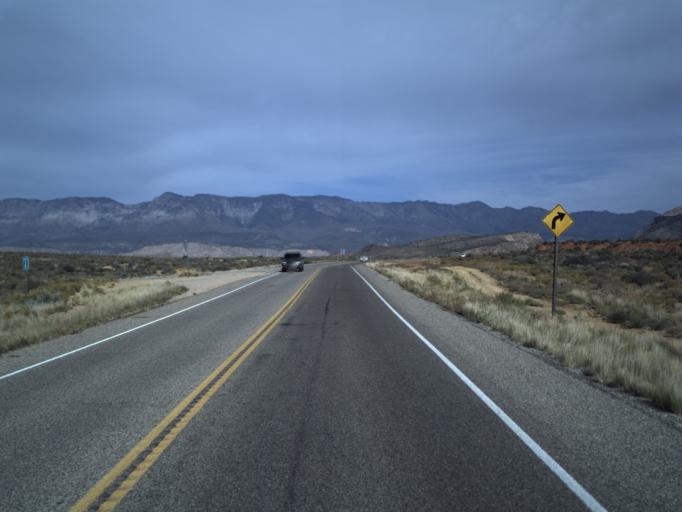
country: US
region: Utah
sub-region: Washington County
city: LaVerkin
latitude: 37.2169
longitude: -113.2485
